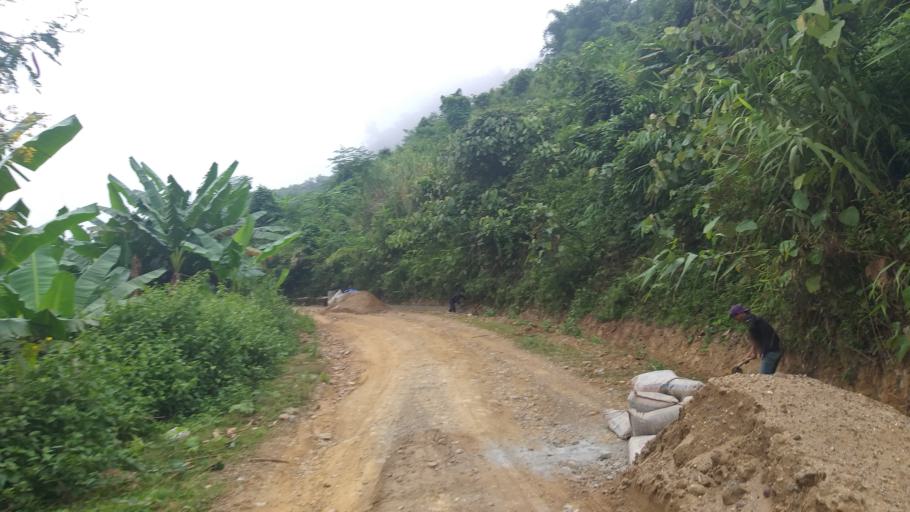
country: LA
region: Phongsali
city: Khoa
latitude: 21.2408
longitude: 102.6708
